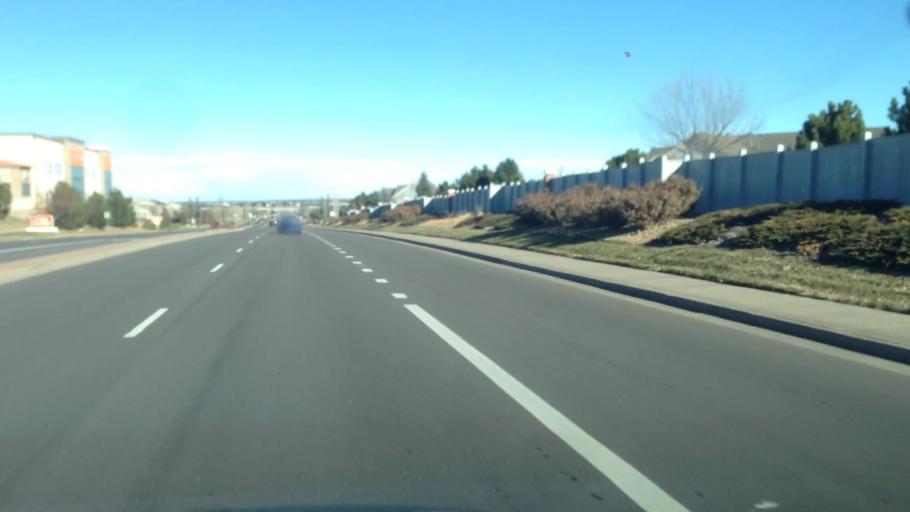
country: US
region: Colorado
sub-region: Douglas County
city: Stonegate
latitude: 39.5371
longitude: -104.7934
